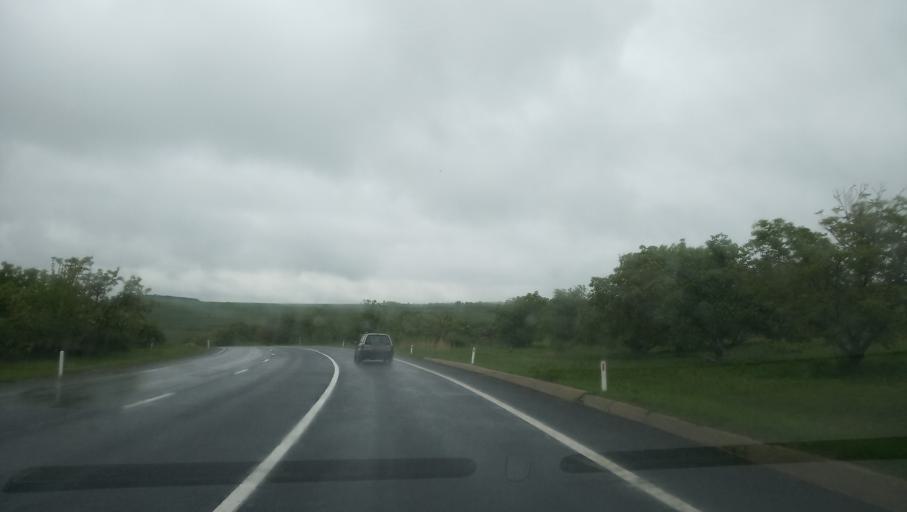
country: RO
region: Sibiu
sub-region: Comuna Apoldu de Jos
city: Apoldu de Jos
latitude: 45.8334
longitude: 23.8562
